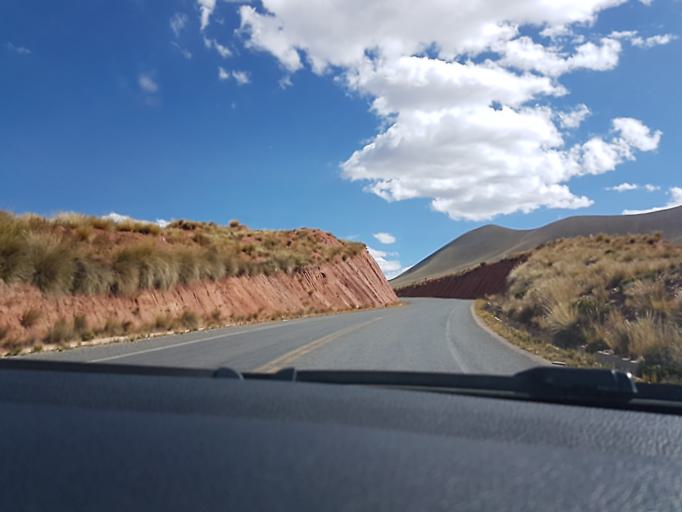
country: BO
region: La Paz
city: Tiahuanaco
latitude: -17.0078
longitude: -68.4275
